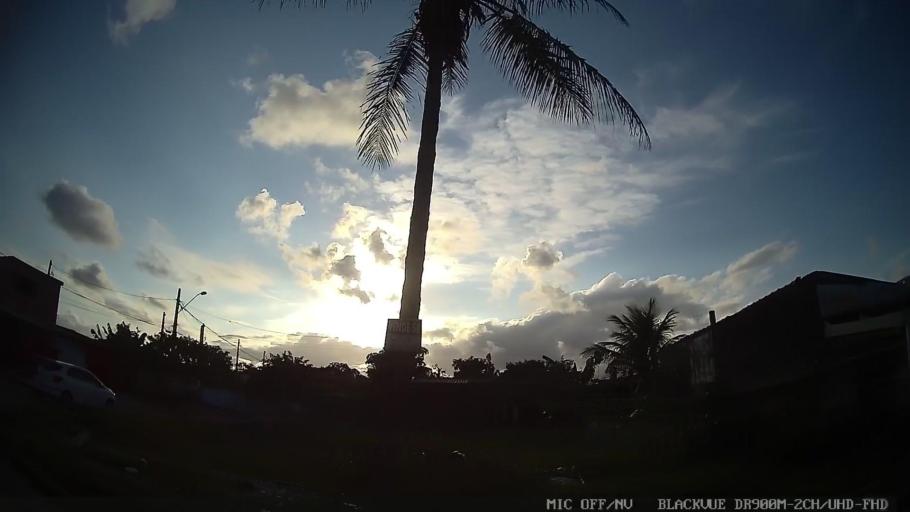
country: BR
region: Sao Paulo
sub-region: Itanhaem
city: Itanhaem
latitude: -24.1813
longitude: -46.8290
